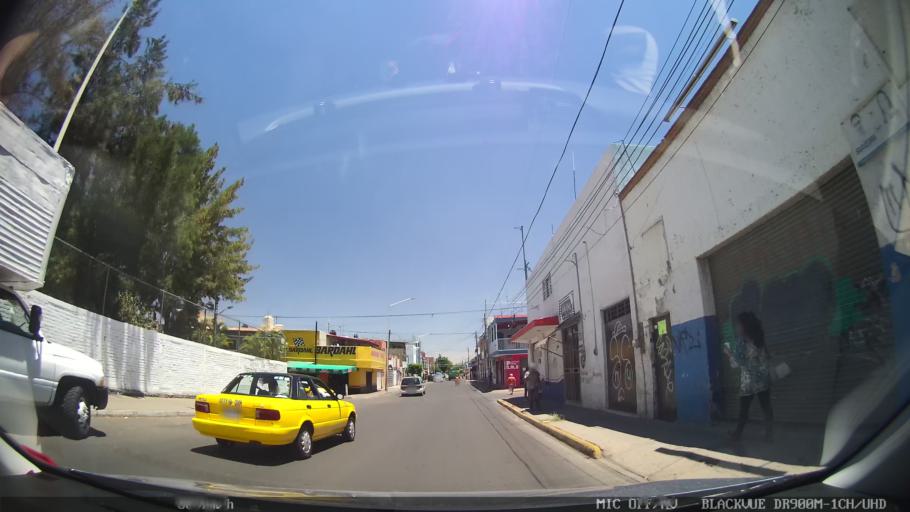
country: MX
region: Jalisco
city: Tlaquepaque
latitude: 20.6583
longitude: -103.2779
